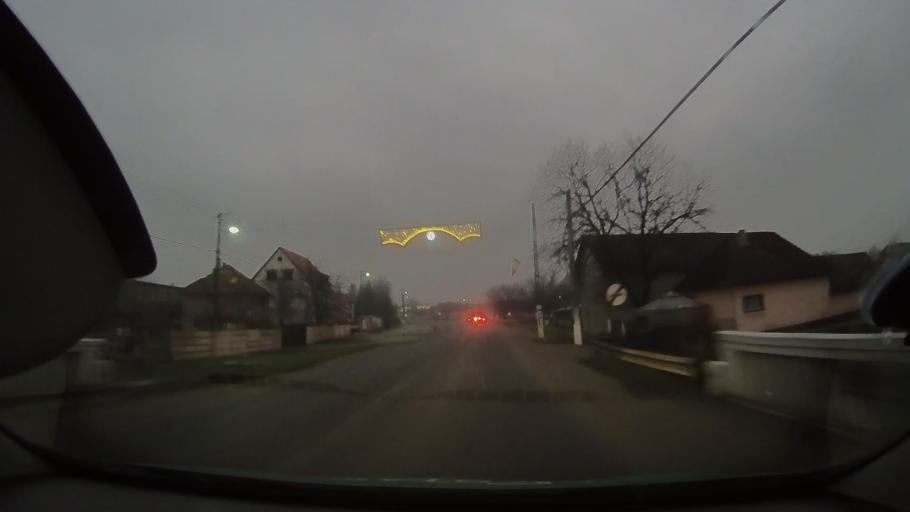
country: RO
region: Arad
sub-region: Comuna Beliu
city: Beliu
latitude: 46.4949
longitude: 21.9803
